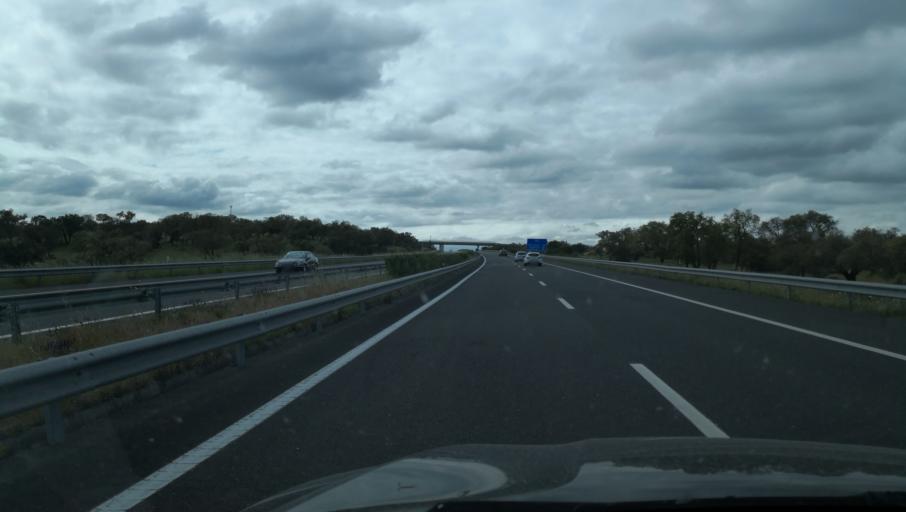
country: PT
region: Santarem
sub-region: Benavente
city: Poceirao
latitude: 38.8422
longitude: -8.7357
